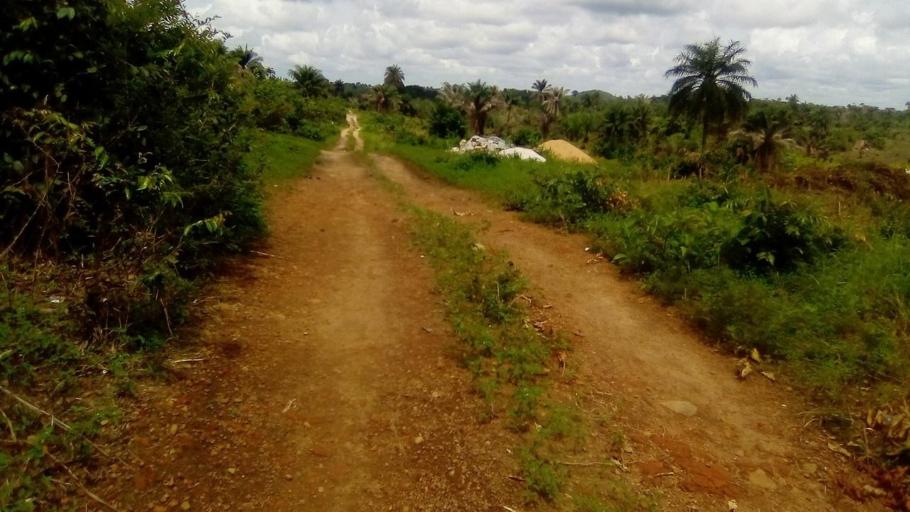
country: SL
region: Southern Province
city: Bo
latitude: 7.9270
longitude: -11.7488
